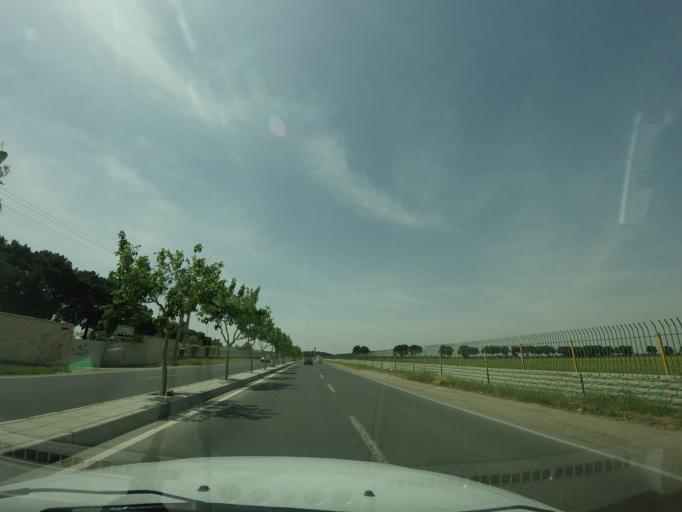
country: IR
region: Tehran
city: Eslamshahr
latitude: 35.5997
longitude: 51.2575
